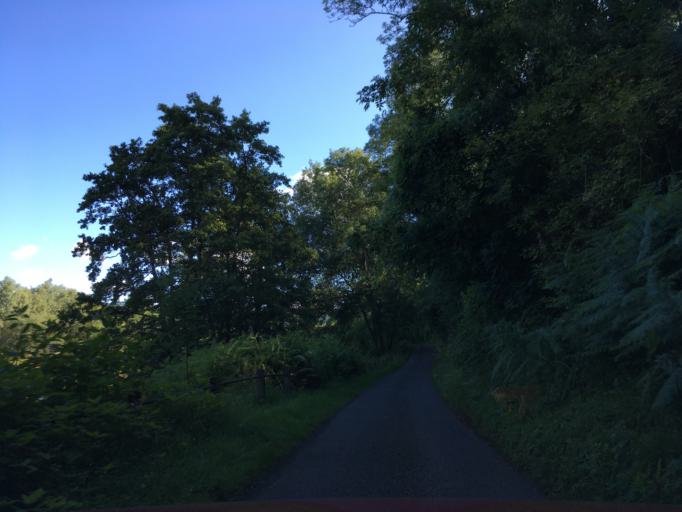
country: GB
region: England
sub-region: Herefordshire
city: Brockhampton
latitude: 51.9568
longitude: -2.5660
